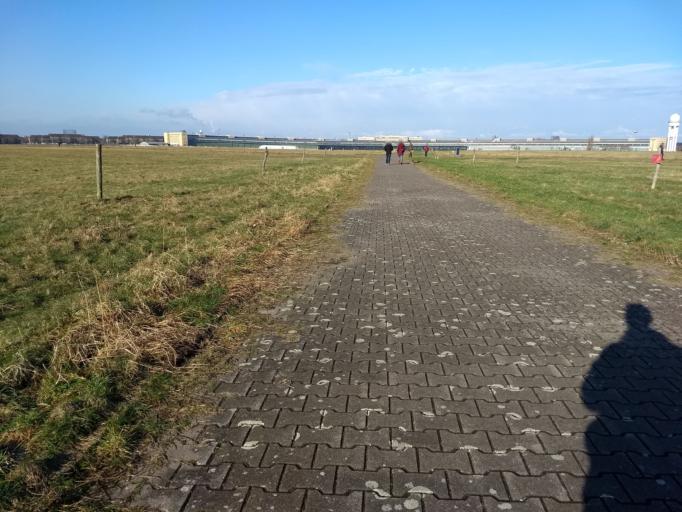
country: DE
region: Berlin
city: Tempelhof Bezirk
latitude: 52.4719
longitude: 13.4035
